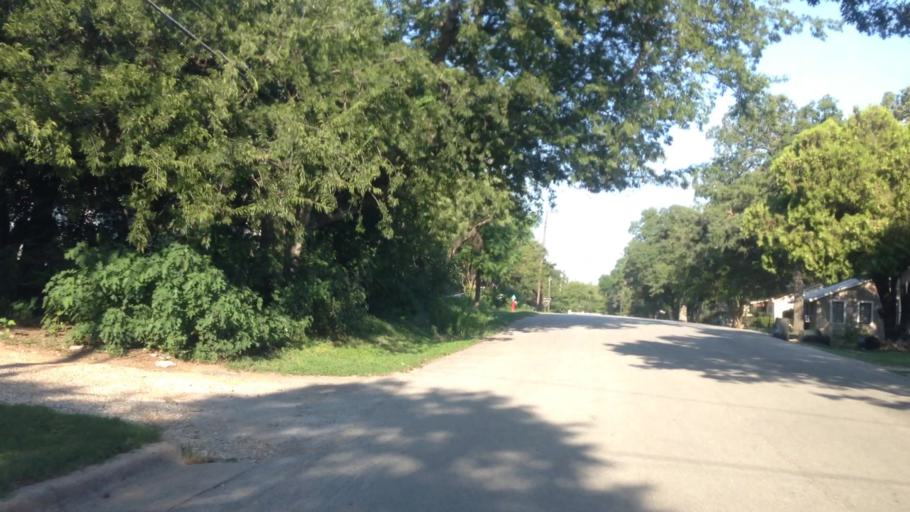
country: US
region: Texas
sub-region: Tarrant County
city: Haltom City
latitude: 32.7999
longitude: -97.2590
